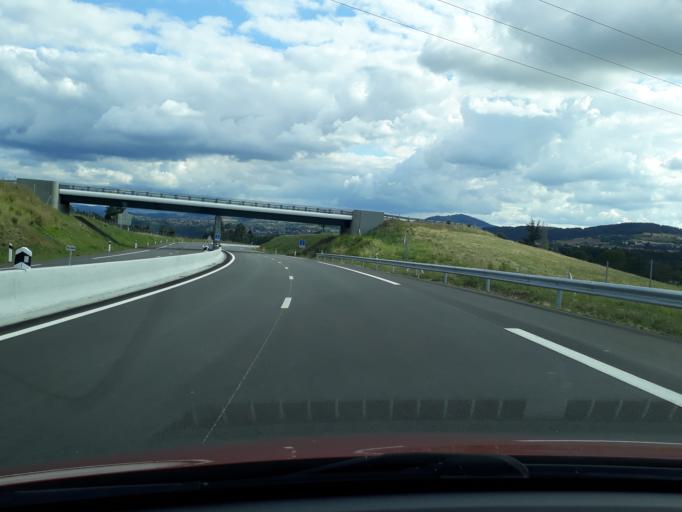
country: FR
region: Auvergne
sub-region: Departement de la Haute-Loire
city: Cussac-sur-Loire
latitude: 45.0094
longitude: 3.8832
